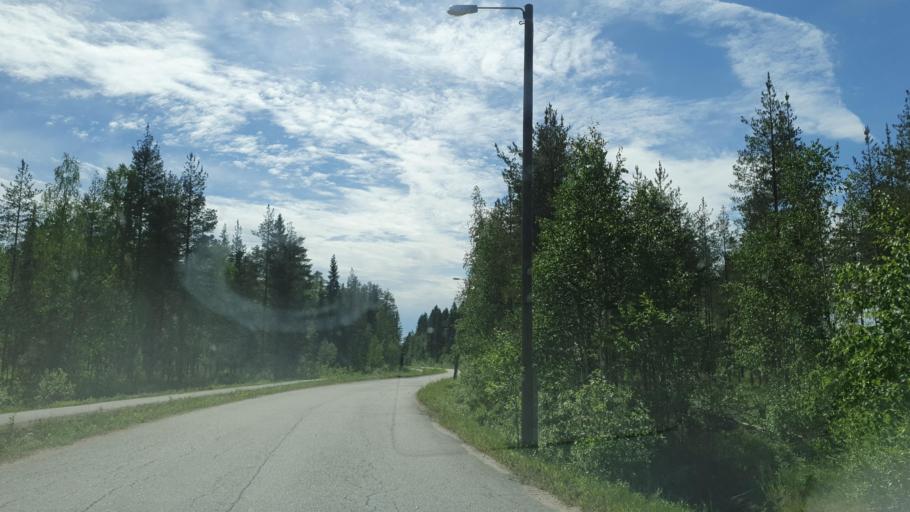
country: FI
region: Kainuu
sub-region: Kehys-Kainuu
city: Hyrynsalmi
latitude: 64.6873
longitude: 28.4679
